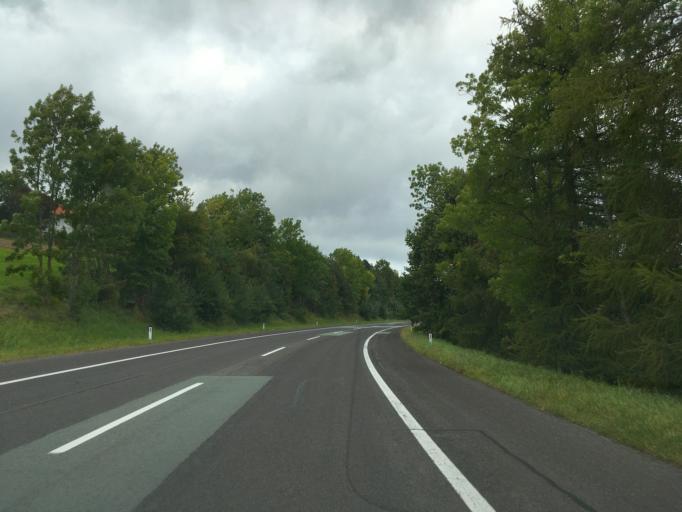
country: AT
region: Lower Austria
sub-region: Politischer Bezirk Neunkirchen
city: Monichkirchen
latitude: 47.4927
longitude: 16.0402
